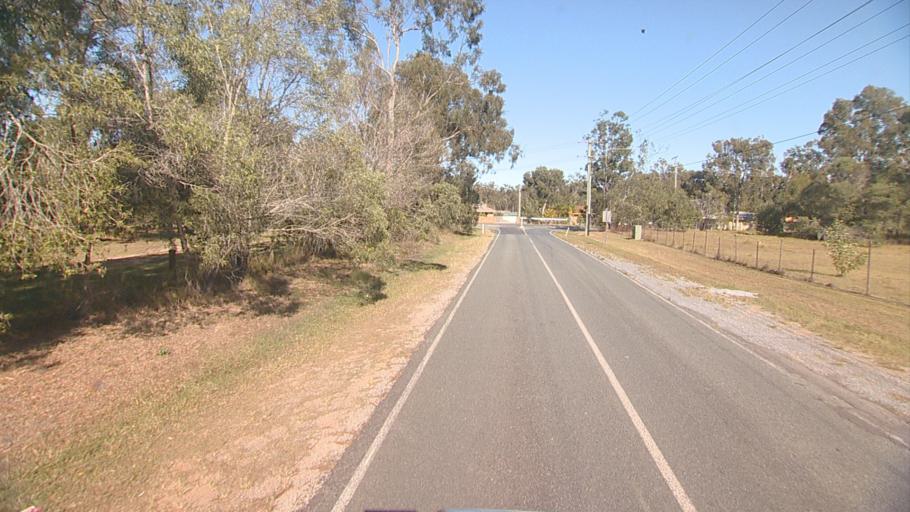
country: AU
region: Queensland
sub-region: Logan
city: Park Ridge South
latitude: -27.7281
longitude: 153.0528
